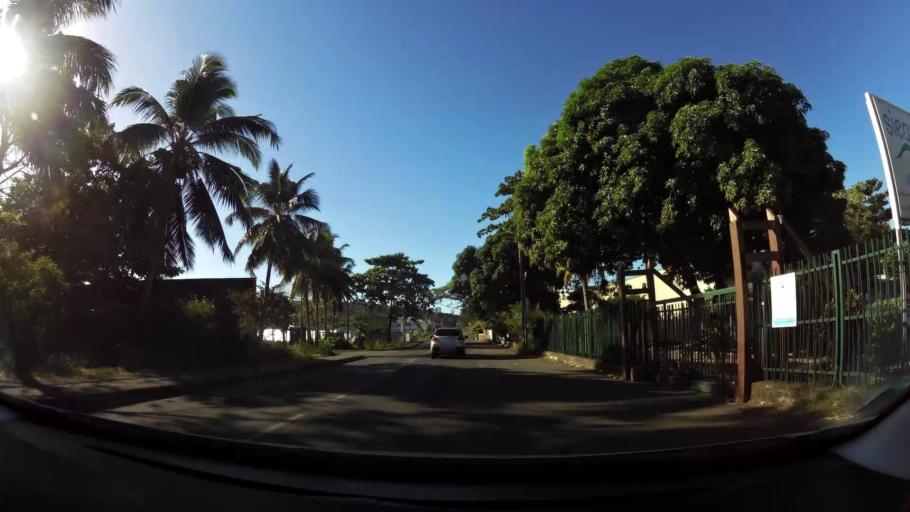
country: YT
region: Mamoudzou
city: Mamoudzou
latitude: -12.7692
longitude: 45.2241
